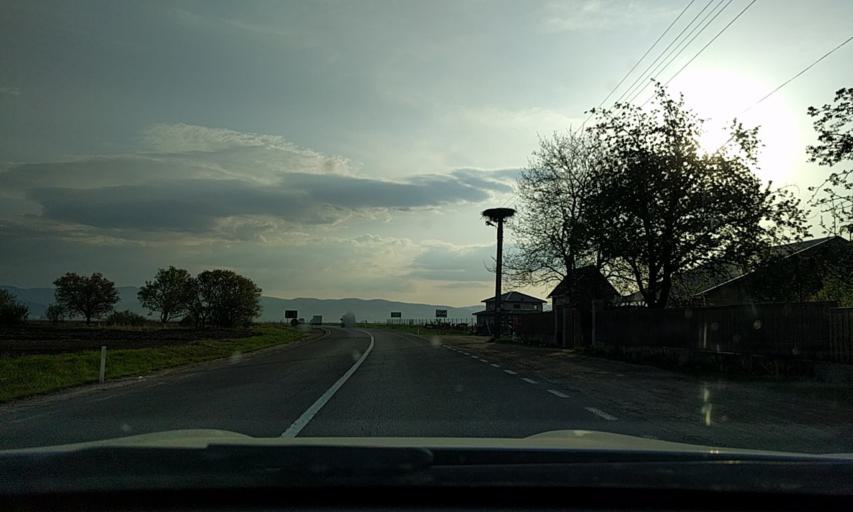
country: RO
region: Covasna
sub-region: Municipiul Targu Secuiesc
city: Lunga
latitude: 46.0308
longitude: 26.2357
